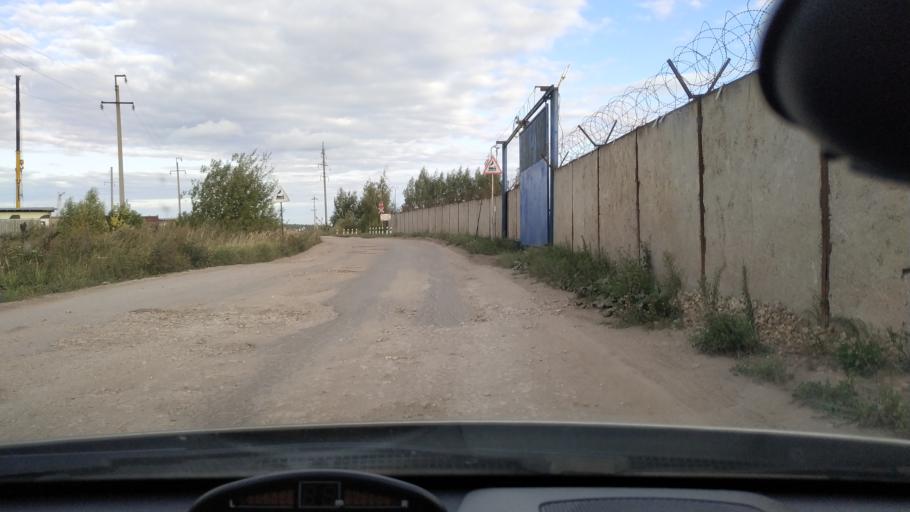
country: RU
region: Rjazan
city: Polyany
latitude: 54.5771
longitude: 39.8433
